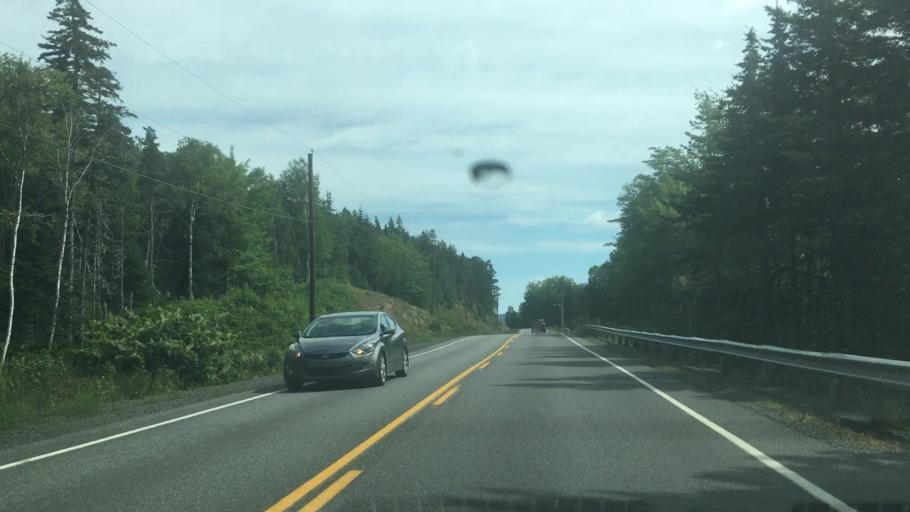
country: CA
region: Nova Scotia
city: Sydney Mines
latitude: 46.2660
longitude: -60.6170
